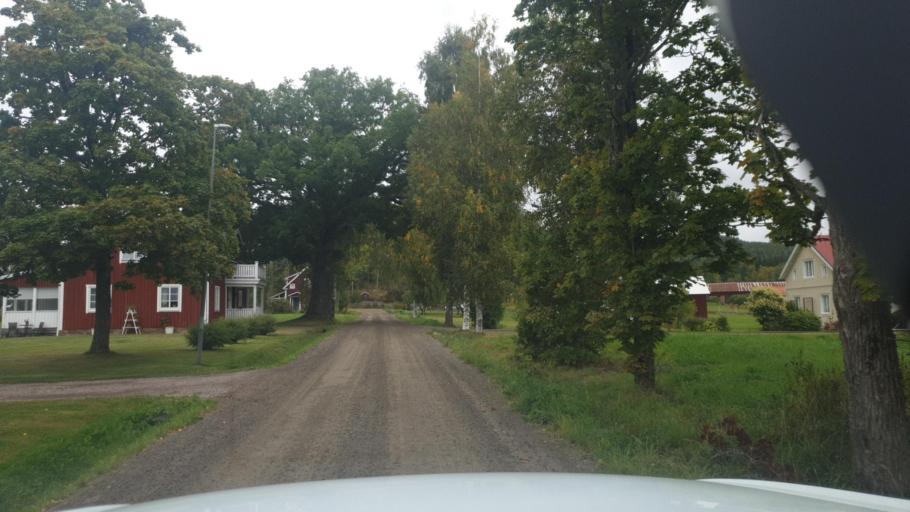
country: SE
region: Vaermland
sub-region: Sunne Kommun
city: Sunne
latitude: 59.8146
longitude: 13.0564
